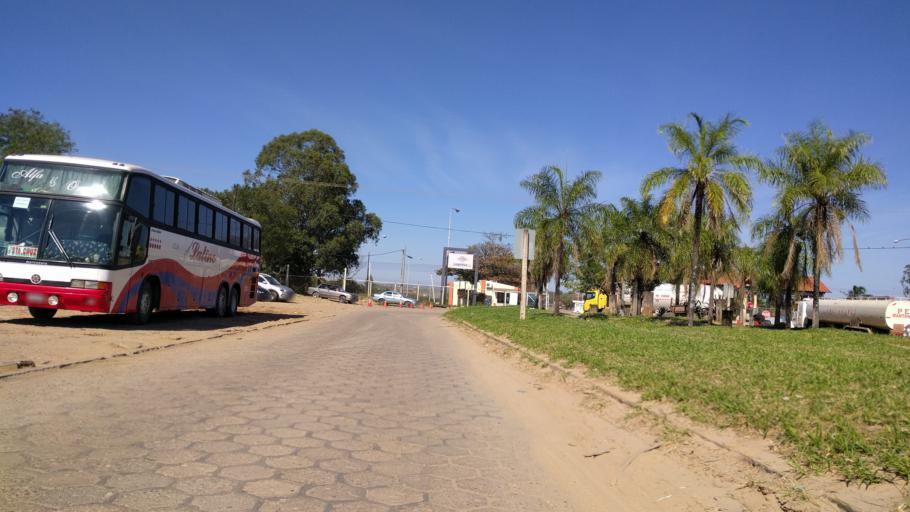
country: BO
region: Santa Cruz
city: Santa Cruz de la Sierra
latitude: -17.8748
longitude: -63.1934
